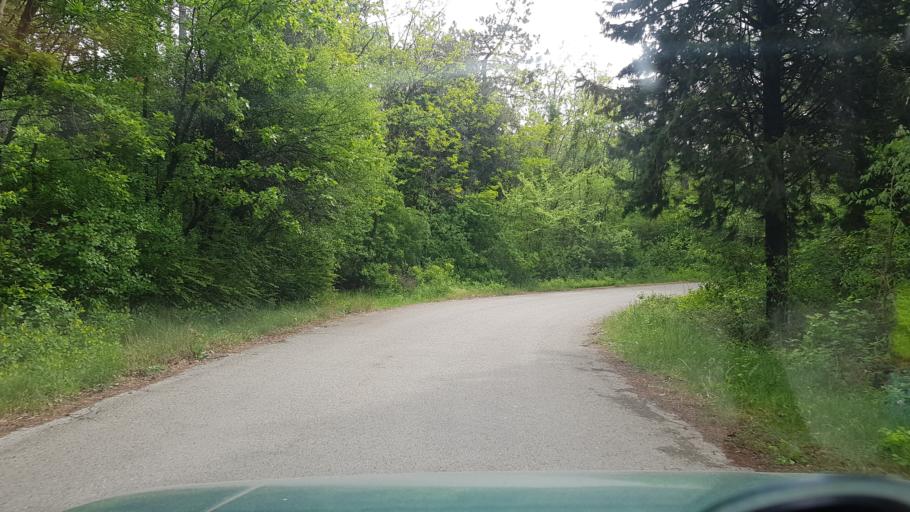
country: IT
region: Friuli Venezia Giulia
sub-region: Provincia di Gorizia
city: Fogliano
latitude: 45.8522
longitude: 13.4949
